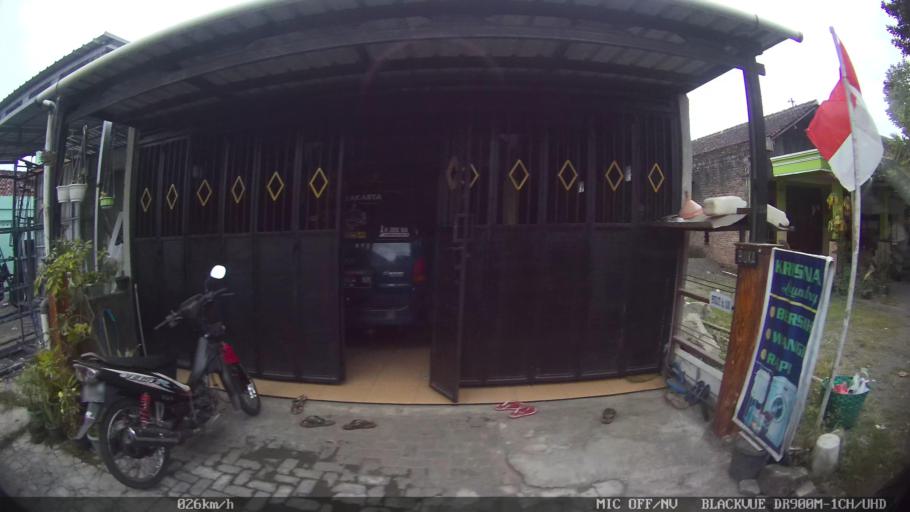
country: ID
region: Daerah Istimewa Yogyakarta
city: Sewon
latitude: -7.8543
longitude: 110.3965
